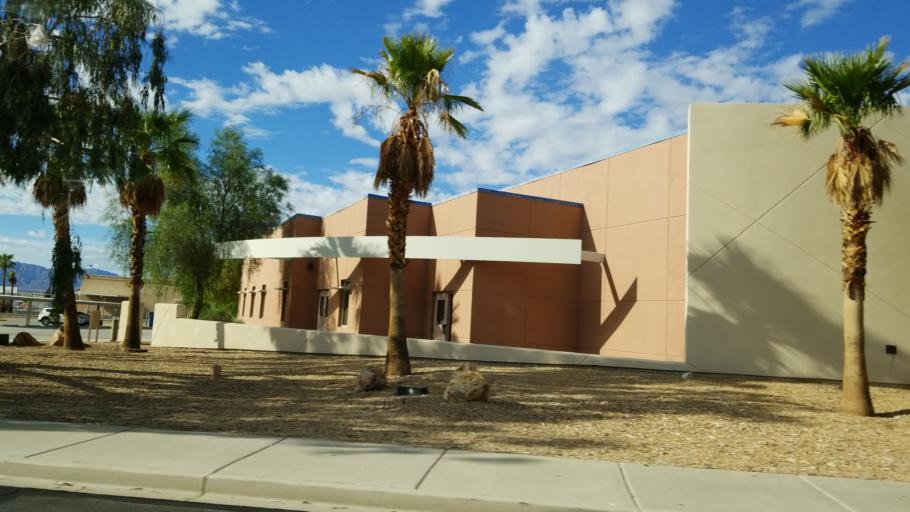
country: US
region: Arizona
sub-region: Mohave County
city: Lake Havasu City
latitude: 34.4772
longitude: -114.3396
